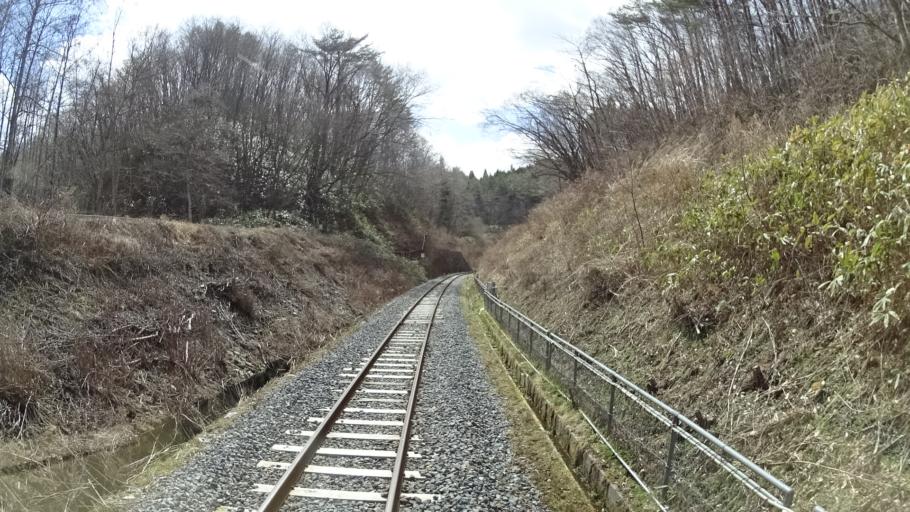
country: JP
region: Iwate
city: Yamada
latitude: 39.4941
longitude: 141.9277
